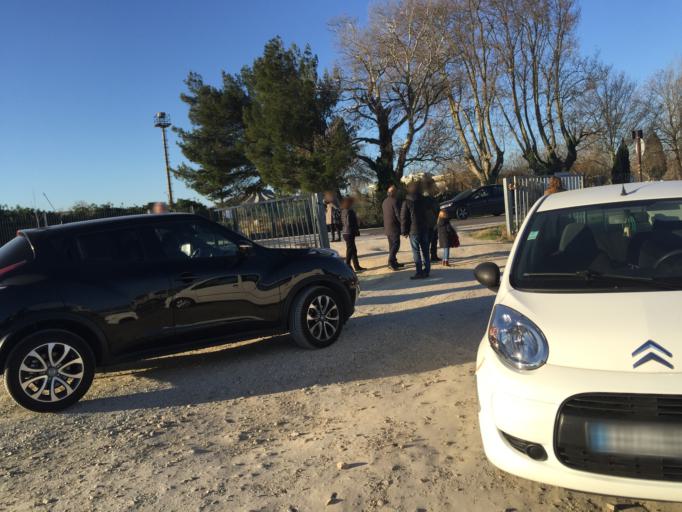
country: FR
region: Provence-Alpes-Cote d'Azur
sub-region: Departement du Vaucluse
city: Montfavet
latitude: 43.9096
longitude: 4.8940
